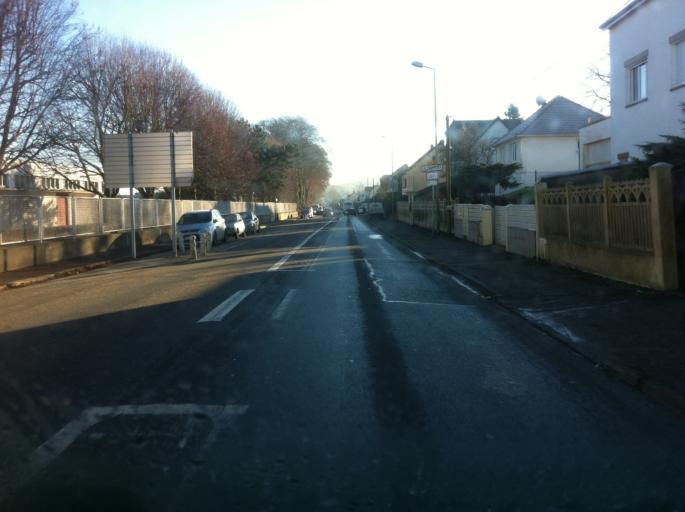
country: FR
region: Picardie
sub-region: Departement de la Somme
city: Mers-les-Bains
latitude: 50.0557
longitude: 1.3886
